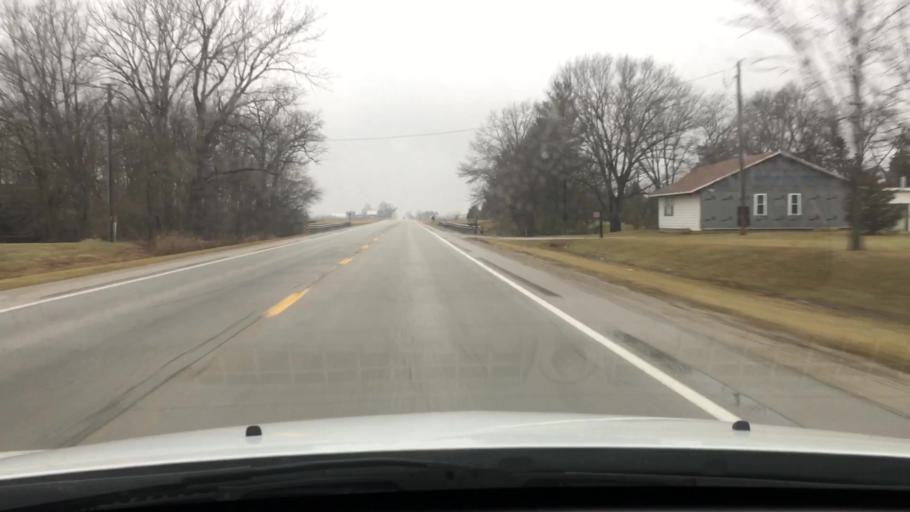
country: US
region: Illinois
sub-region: Livingston County
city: Pontiac
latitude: 40.8728
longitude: -88.7271
